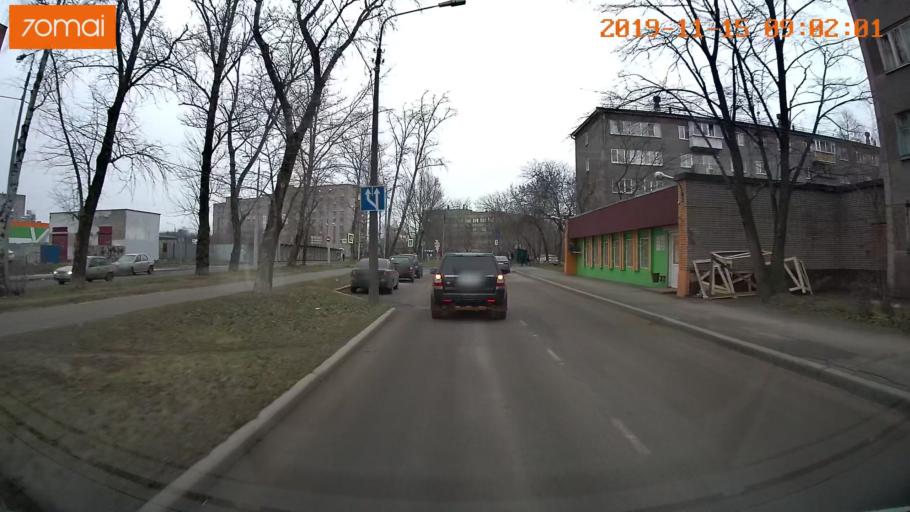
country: RU
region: Vologda
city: Cherepovets
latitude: 59.1351
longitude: 37.9271
